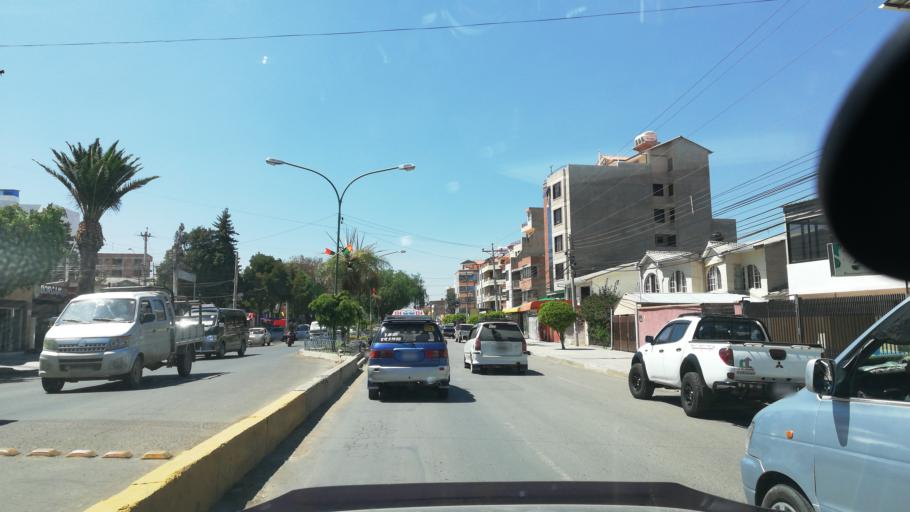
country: BO
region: Cochabamba
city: Cochabamba
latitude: -17.3608
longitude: -66.1865
